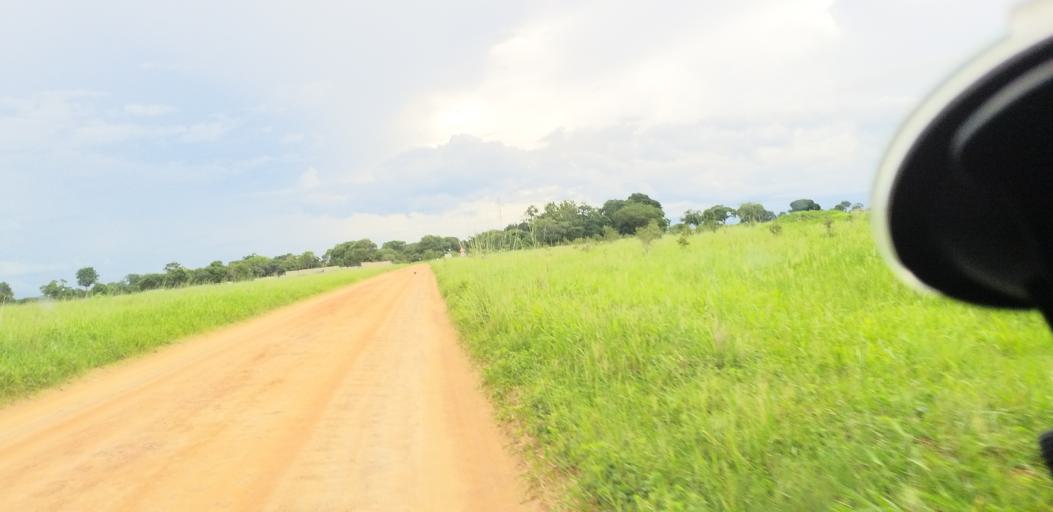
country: ZM
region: Lusaka
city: Chongwe
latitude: -15.1586
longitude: 28.4883
